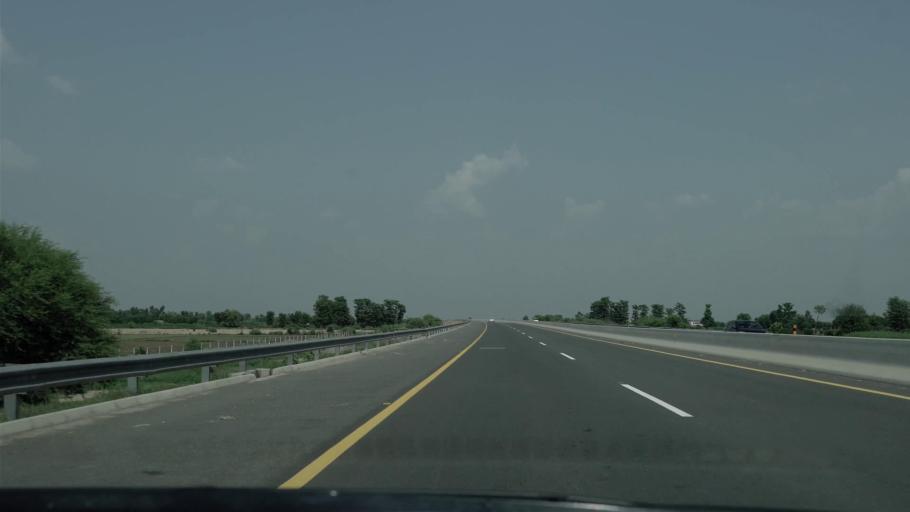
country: PK
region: Punjab
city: Gojra
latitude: 31.1920
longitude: 72.6507
